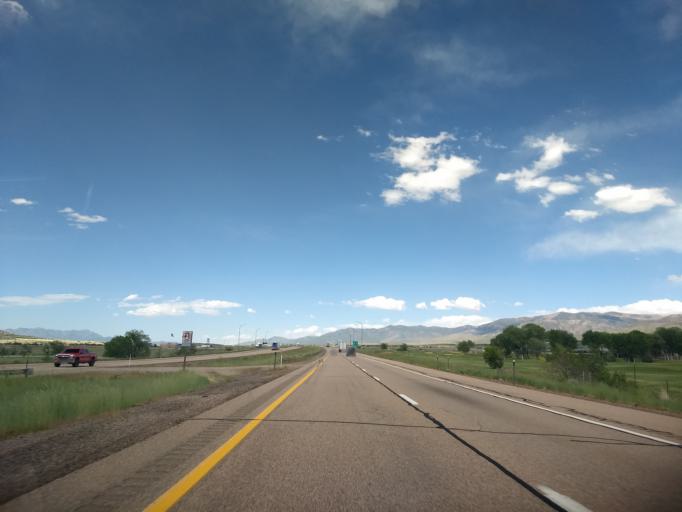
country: US
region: Utah
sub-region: Millard County
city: Fillmore
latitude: 38.9868
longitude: -112.3294
